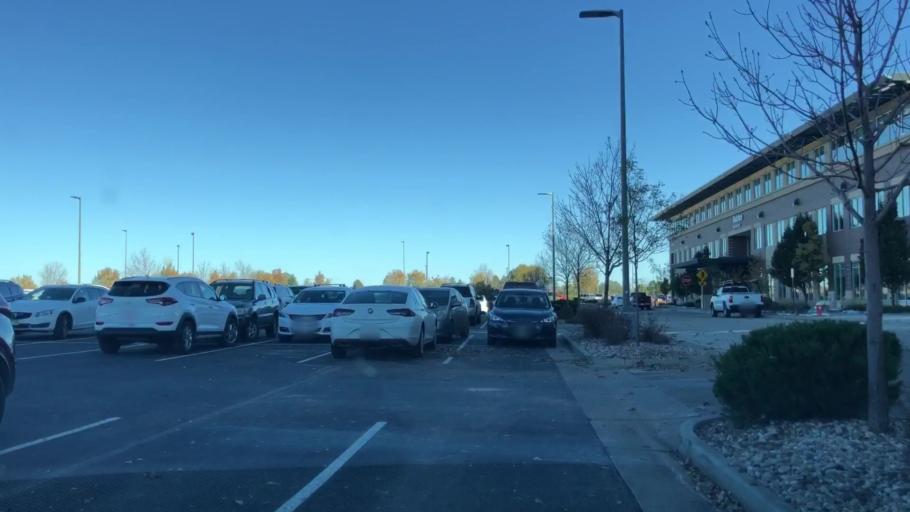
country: US
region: Colorado
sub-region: Larimer County
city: Loveland
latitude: 40.4225
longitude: -105.0039
